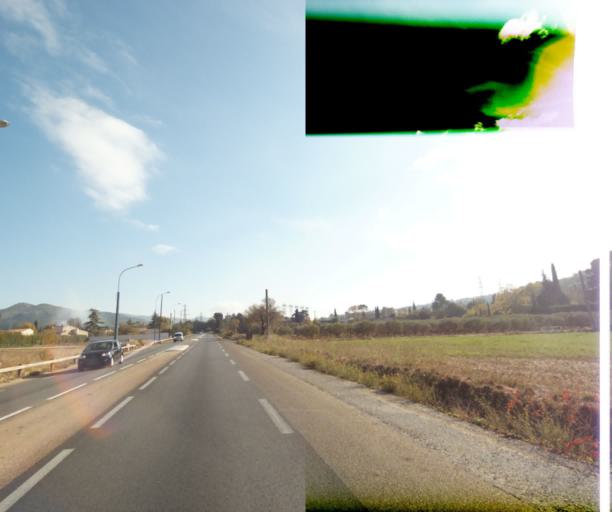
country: FR
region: Provence-Alpes-Cote d'Azur
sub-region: Departement des Bouches-du-Rhone
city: Allauch
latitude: 43.3238
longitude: 5.4752
